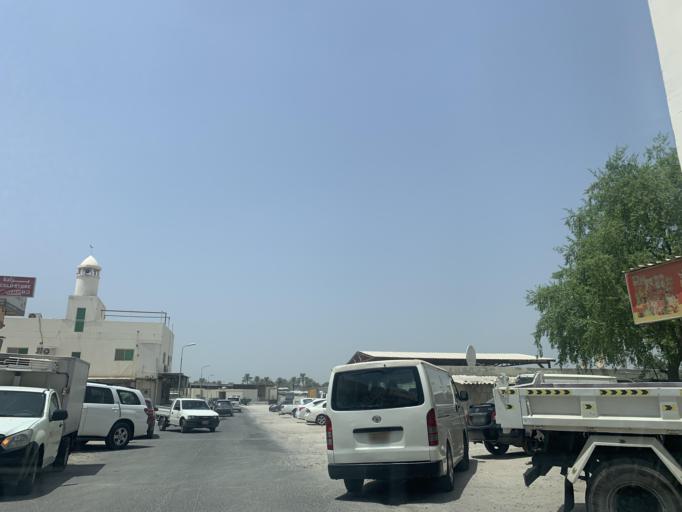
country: BH
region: Central Governorate
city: Madinat Hamad
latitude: 26.1496
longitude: 50.5011
